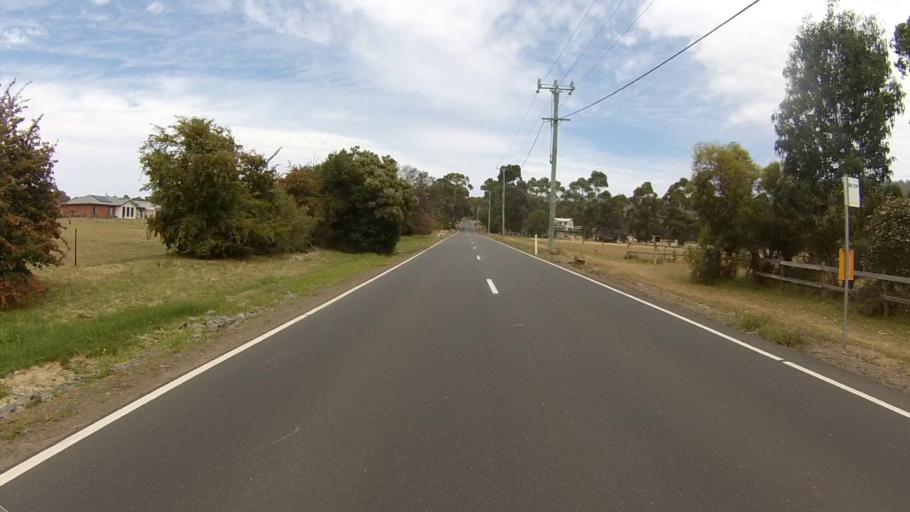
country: AU
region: Tasmania
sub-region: Clarence
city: Acton Park
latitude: -42.8647
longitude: 147.4900
